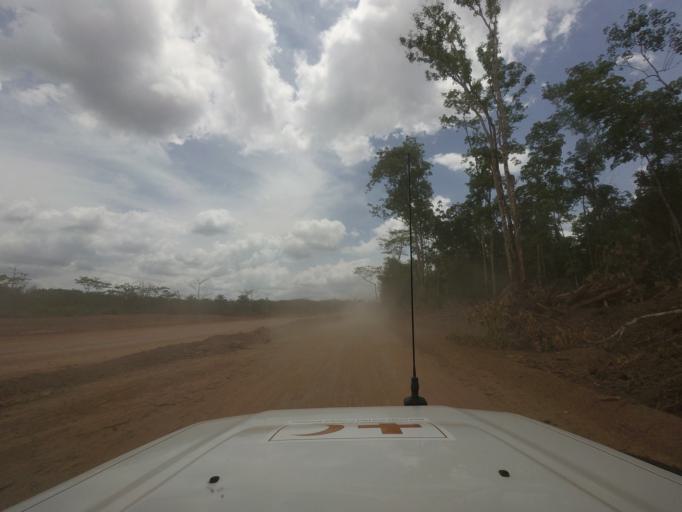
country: LR
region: Nimba
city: Sanniquellie
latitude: 7.2509
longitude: -8.8588
